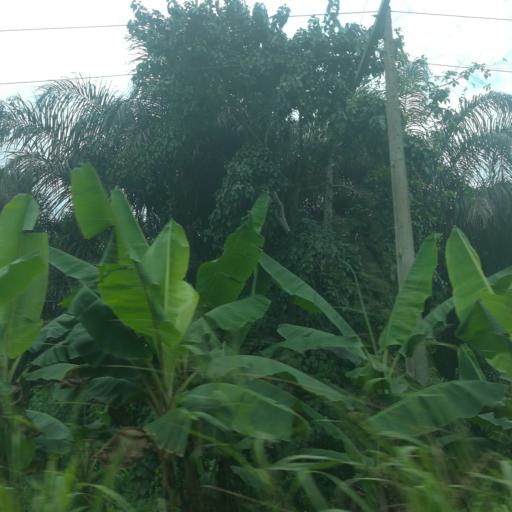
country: NG
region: Lagos
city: Ejirin
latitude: 6.6508
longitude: 3.7890
